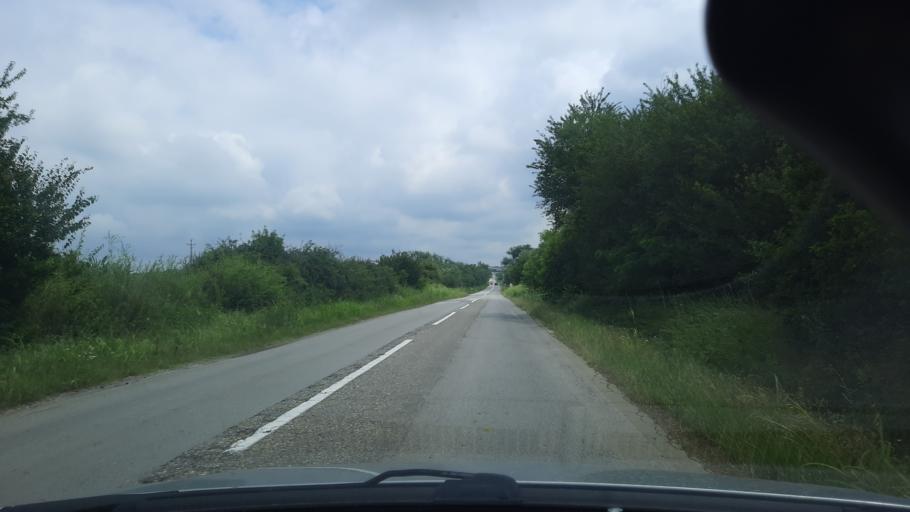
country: RS
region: Central Serbia
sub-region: Branicevski Okrug
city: Malo Crnice
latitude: 44.5767
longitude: 21.3402
